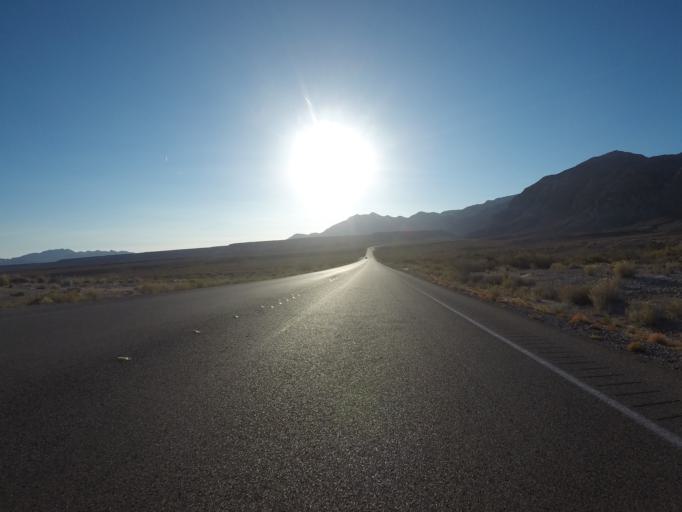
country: US
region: Nevada
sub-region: Clark County
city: Moapa Valley
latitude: 36.3695
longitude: -114.4459
